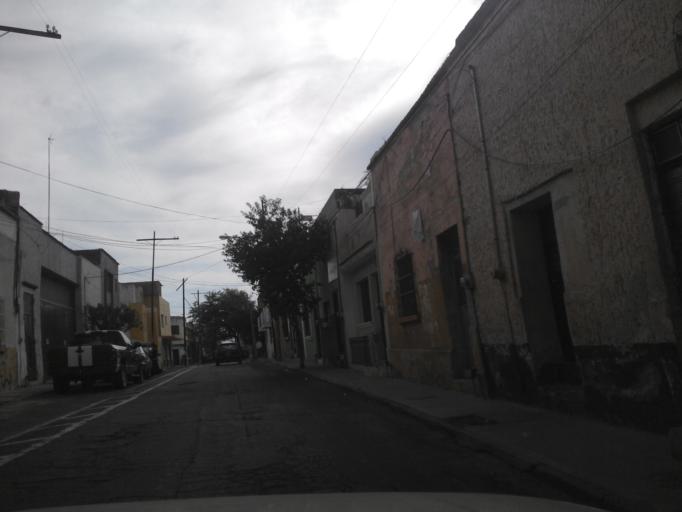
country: MX
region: Jalisco
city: Guadalajara
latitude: 20.6683
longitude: -103.3529
